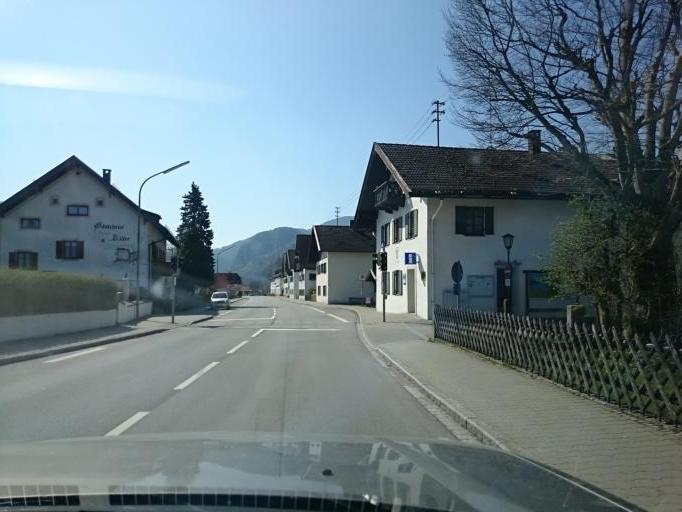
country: DE
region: Bavaria
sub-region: Upper Bavaria
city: Schlehdorf
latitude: 47.6577
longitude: 11.3153
